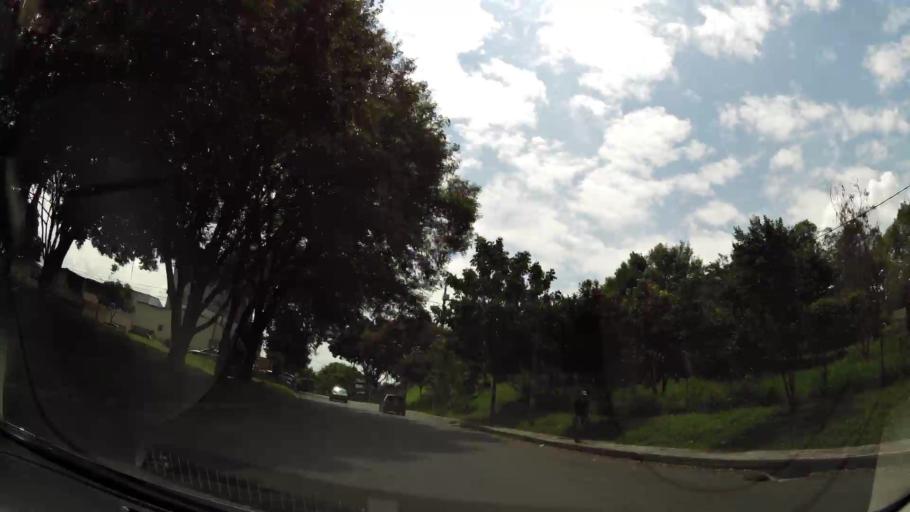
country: CO
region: Antioquia
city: Medellin
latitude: 6.2479
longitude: -75.6162
